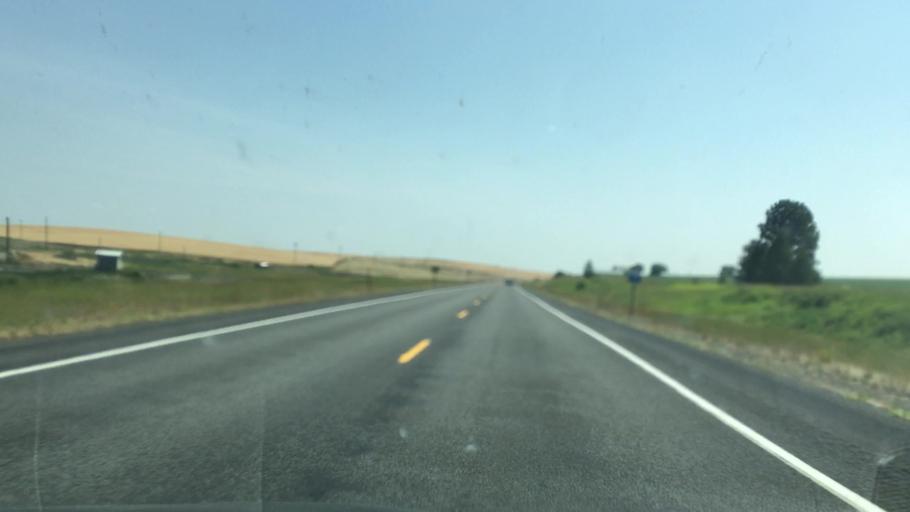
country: US
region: Idaho
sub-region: Lewis County
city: Nezperce
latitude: 46.2305
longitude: -116.4592
